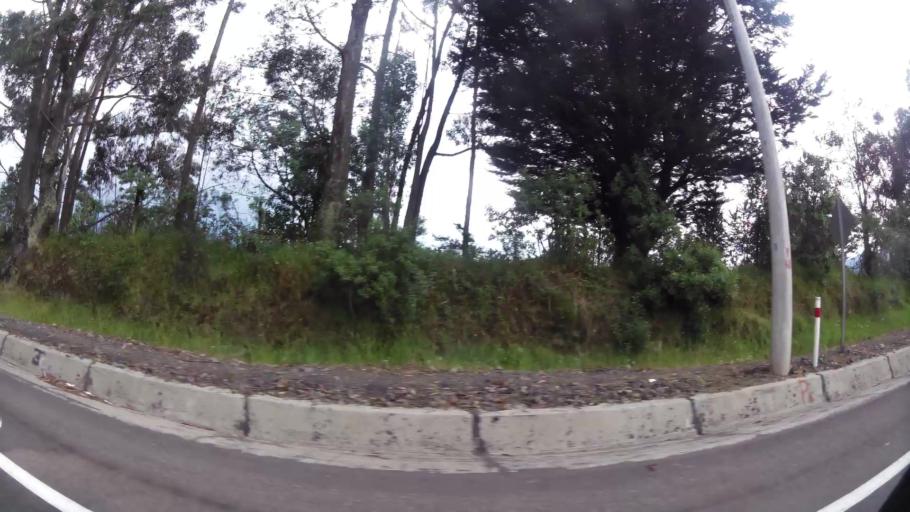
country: EC
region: Pichincha
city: Sangolqui
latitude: -0.3903
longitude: -78.5463
